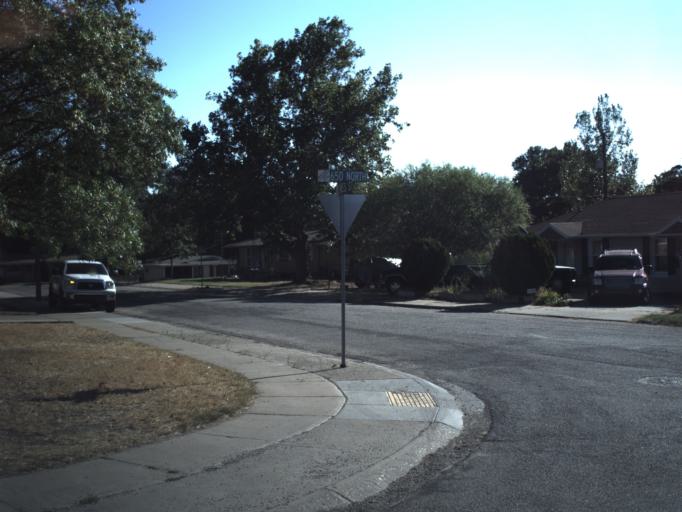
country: US
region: Utah
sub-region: Davis County
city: Clearfield
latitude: 41.1230
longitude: -112.0276
